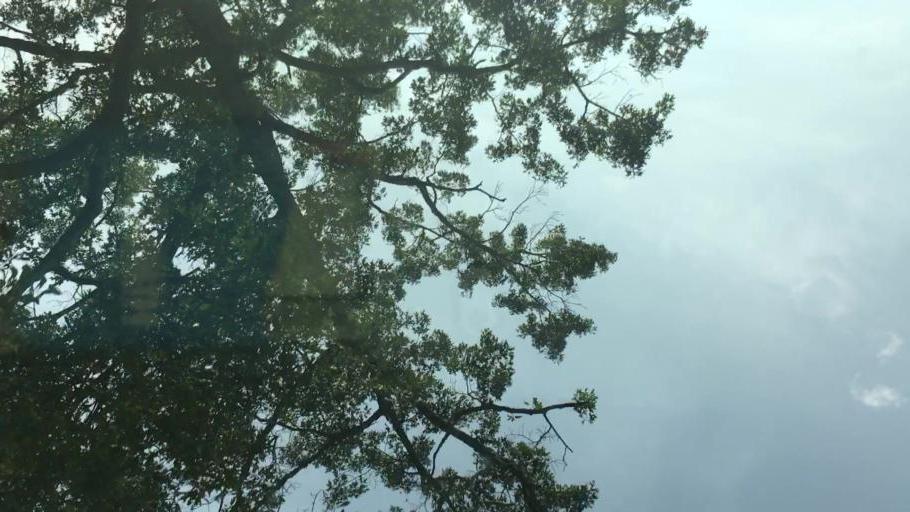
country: US
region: Alabama
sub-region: Bibb County
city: Woodstock
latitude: 33.2184
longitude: -87.1129
